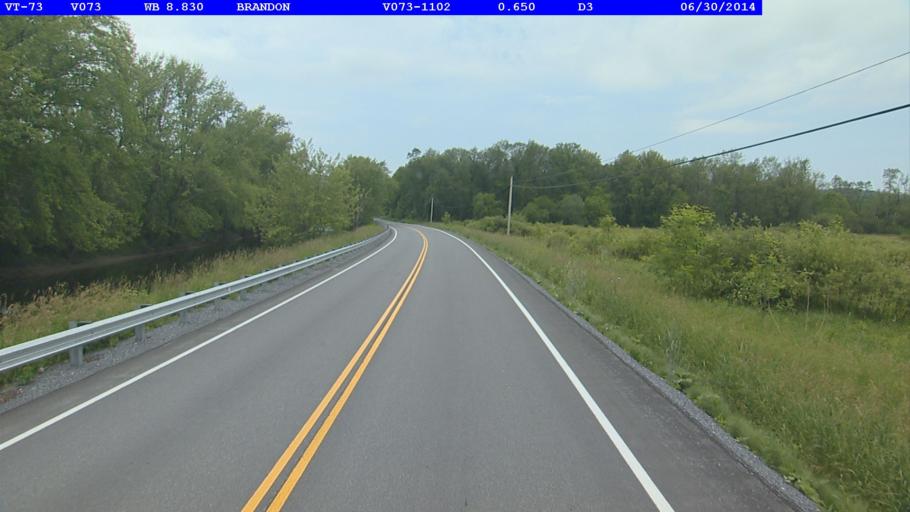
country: US
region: Vermont
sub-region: Rutland County
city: Brandon
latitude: 43.8061
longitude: -73.1348
